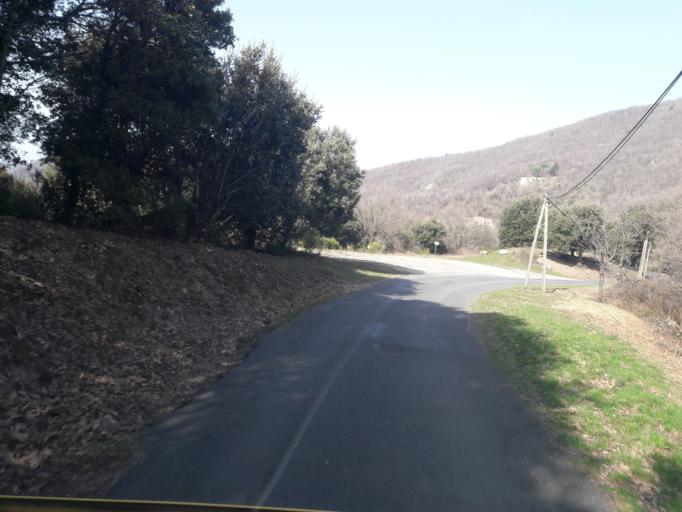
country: FR
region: Languedoc-Roussillon
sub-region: Departement du Gard
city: Sumene
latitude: 44.0100
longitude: 3.7784
